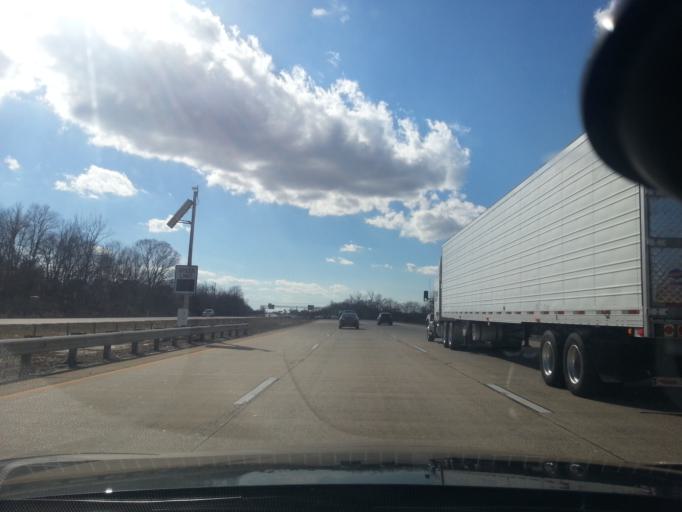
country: US
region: Delaware
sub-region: New Castle County
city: Wilmington
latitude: 39.7171
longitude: -75.5655
